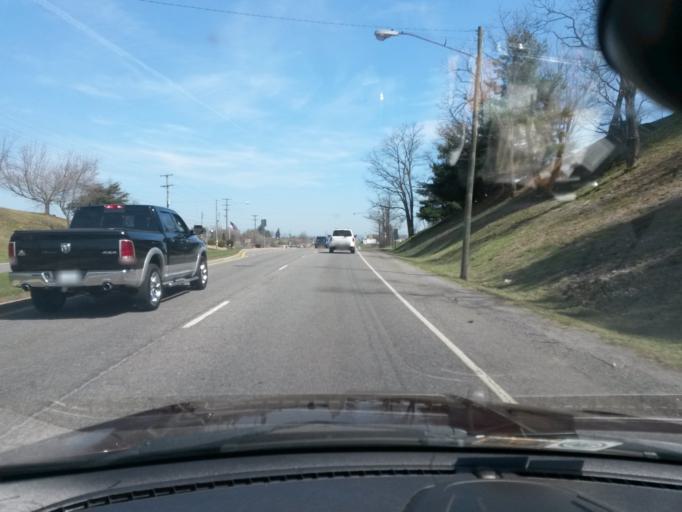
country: US
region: Virginia
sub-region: Montgomery County
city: Christiansburg
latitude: 37.1457
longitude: -80.4152
